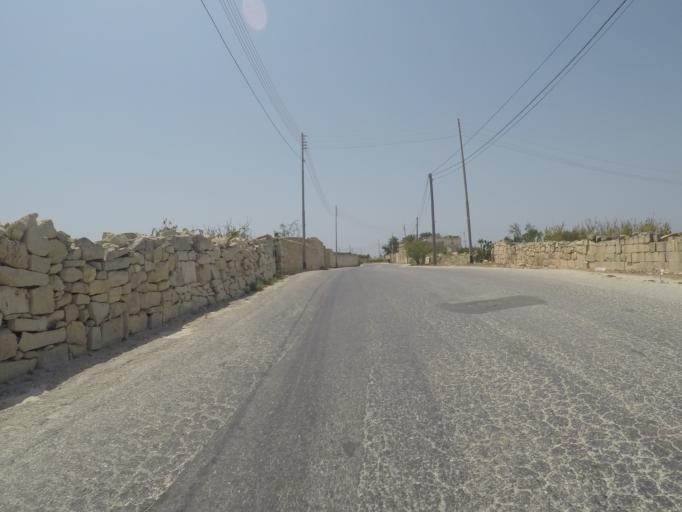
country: MT
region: Is-Siggiewi
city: Siggiewi
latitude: 35.8391
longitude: 14.4291
